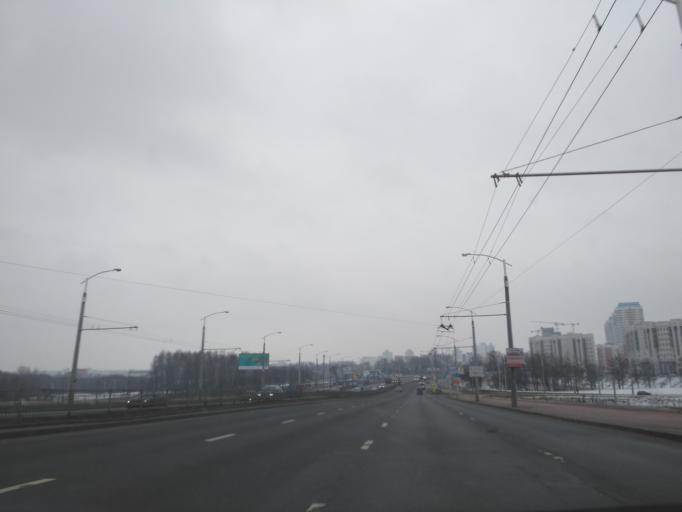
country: BY
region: Minsk
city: Novoye Medvezhino
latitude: 53.8740
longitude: 27.4950
